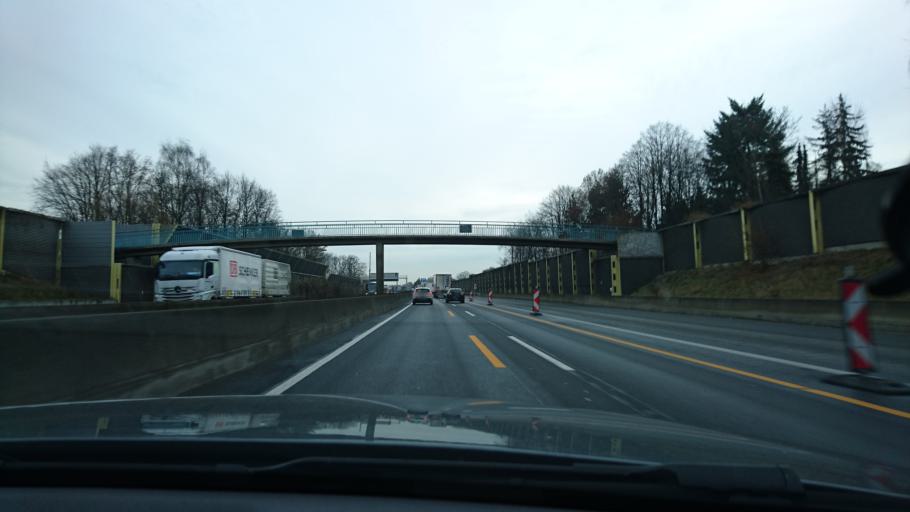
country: DE
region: North Rhine-Westphalia
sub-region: Regierungsbezirk Munster
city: Lotte
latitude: 52.2862
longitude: 7.9390
